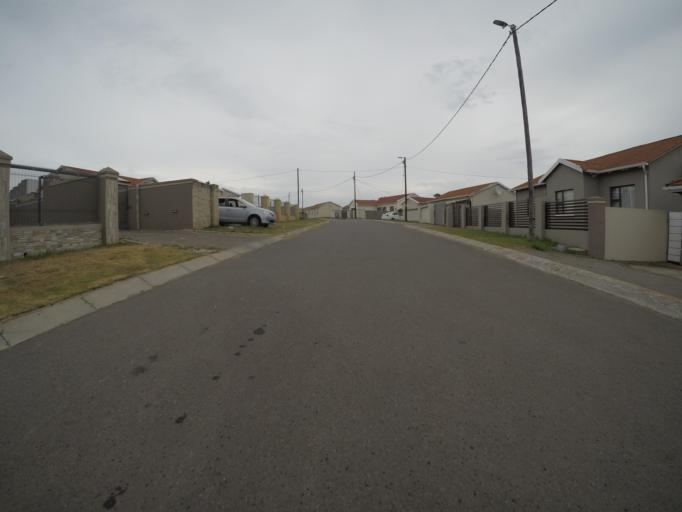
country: ZA
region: Eastern Cape
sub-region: Buffalo City Metropolitan Municipality
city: East London
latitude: -33.0029
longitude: 27.8518
